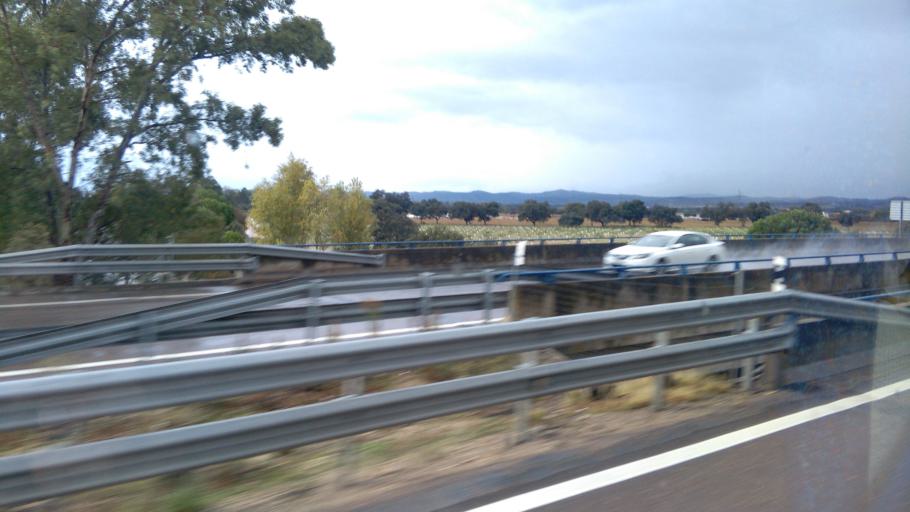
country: ES
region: Castille-La Mancha
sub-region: Province of Toledo
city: Cervera de los Montes
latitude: 39.9959
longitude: -4.7632
